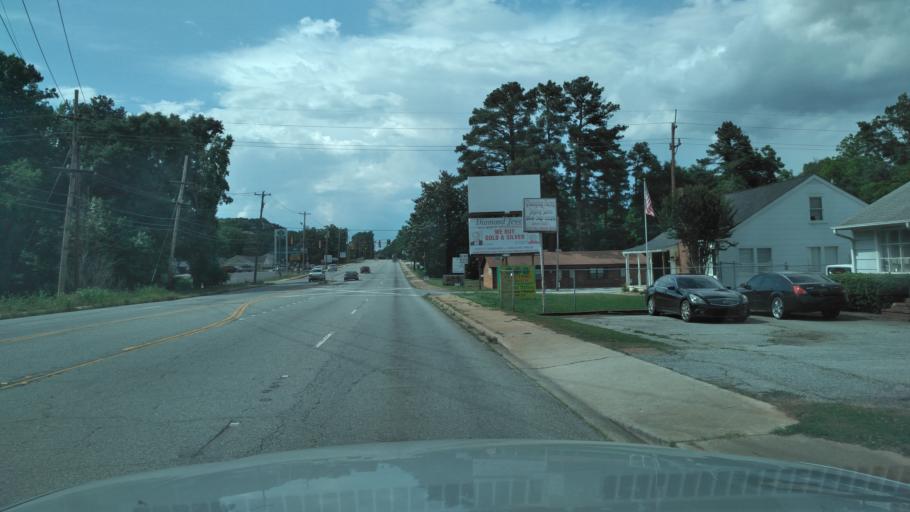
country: US
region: South Carolina
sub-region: Spartanburg County
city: Saxon
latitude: 34.9812
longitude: -81.9443
